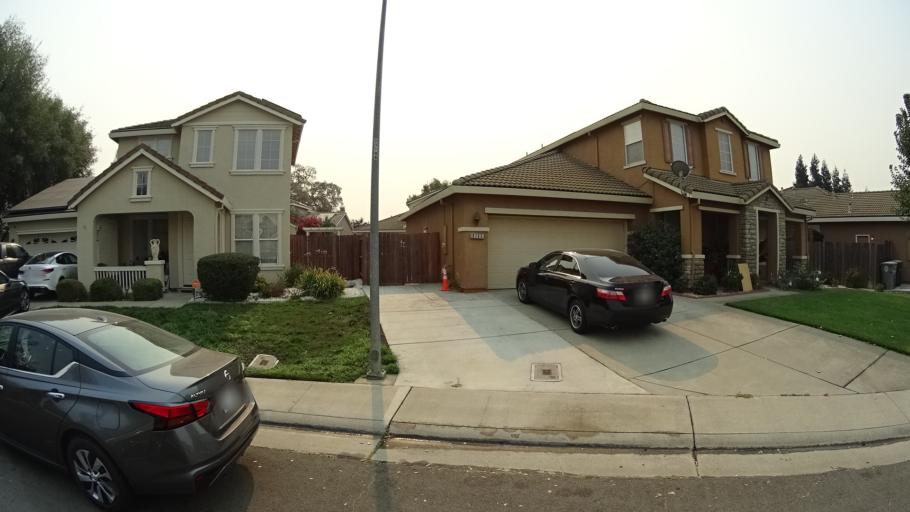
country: US
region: California
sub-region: Sacramento County
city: Laguna
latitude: 38.4048
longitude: -121.4495
